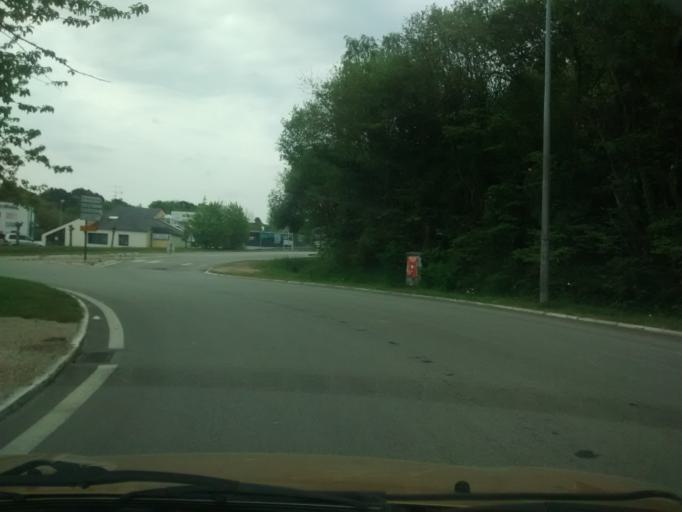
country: FR
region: Brittany
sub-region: Departement du Morbihan
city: Muzillac
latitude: 47.5588
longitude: -2.4986
